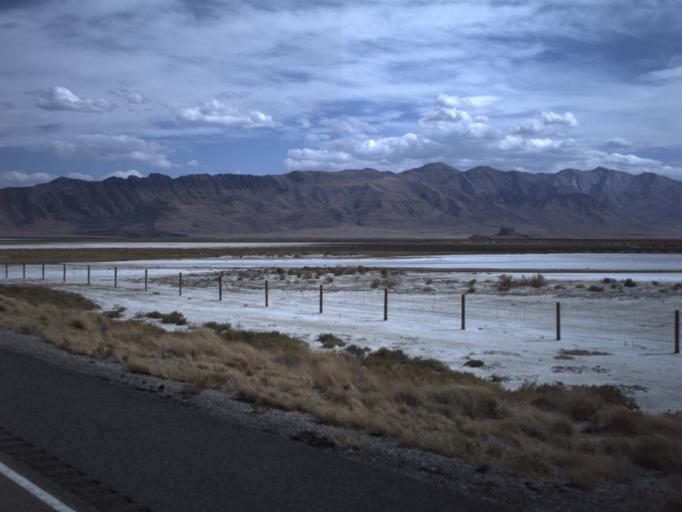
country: US
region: Utah
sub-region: Tooele County
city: Grantsville
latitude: 40.7527
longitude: -112.7239
